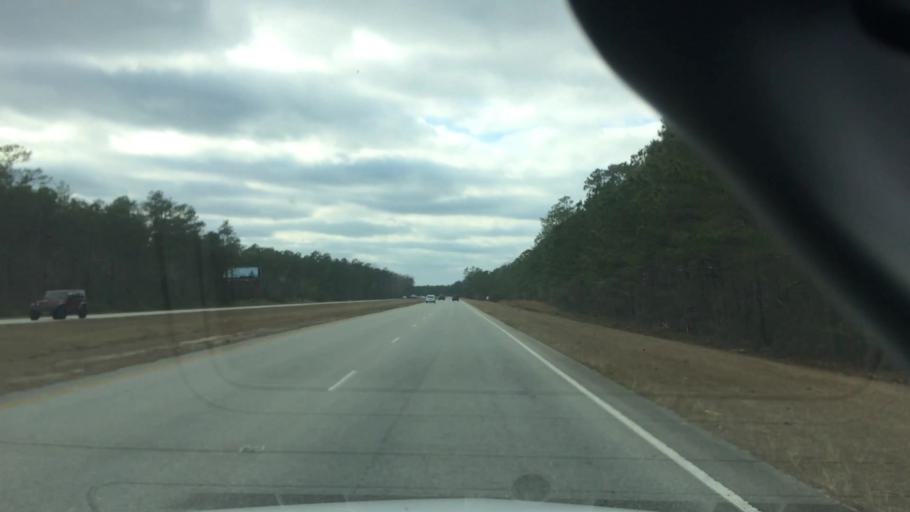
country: US
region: North Carolina
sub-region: Brunswick County
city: Bolivia
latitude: 34.0777
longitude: -78.1467
